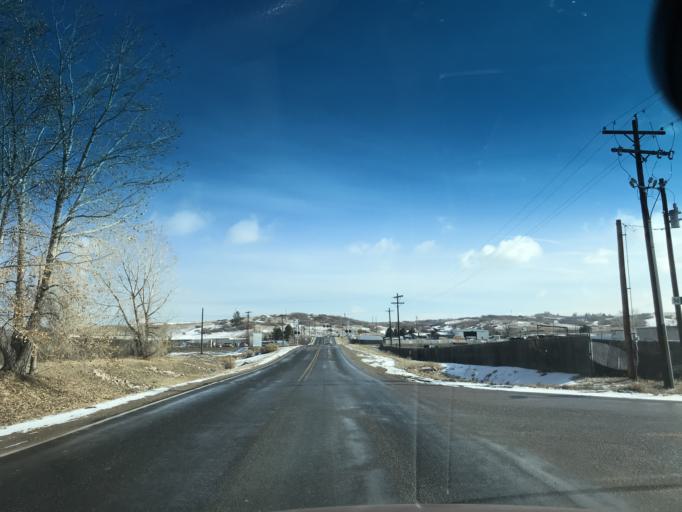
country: US
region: Colorado
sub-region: Douglas County
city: Highlands Ranch
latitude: 39.4710
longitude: -104.9930
